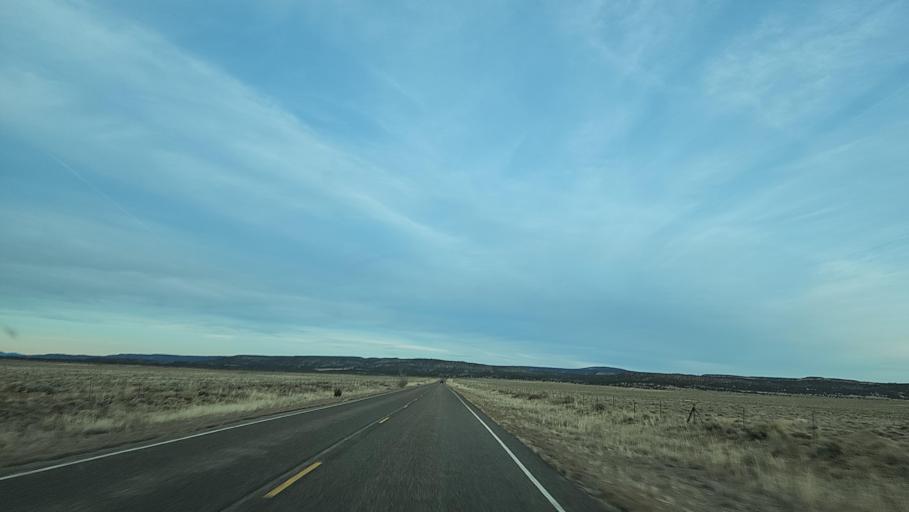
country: US
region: New Mexico
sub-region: Cibola County
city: Grants
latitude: 34.7052
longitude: -108.0194
